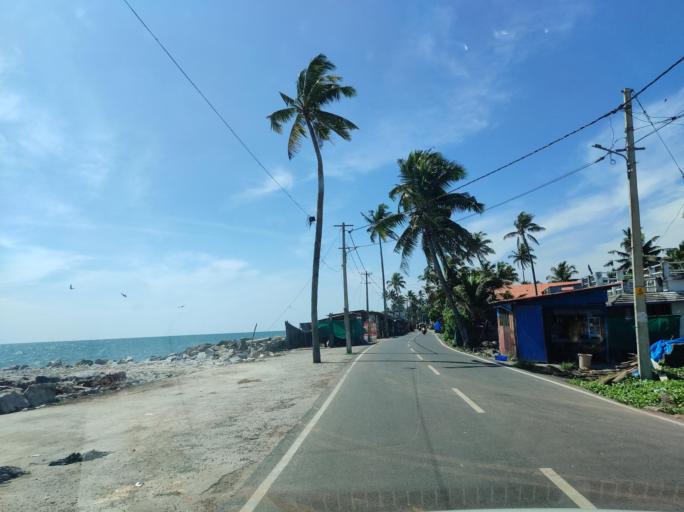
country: IN
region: Kerala
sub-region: Alappuzha
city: Kayankulam
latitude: 9.2153
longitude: 76.4273
